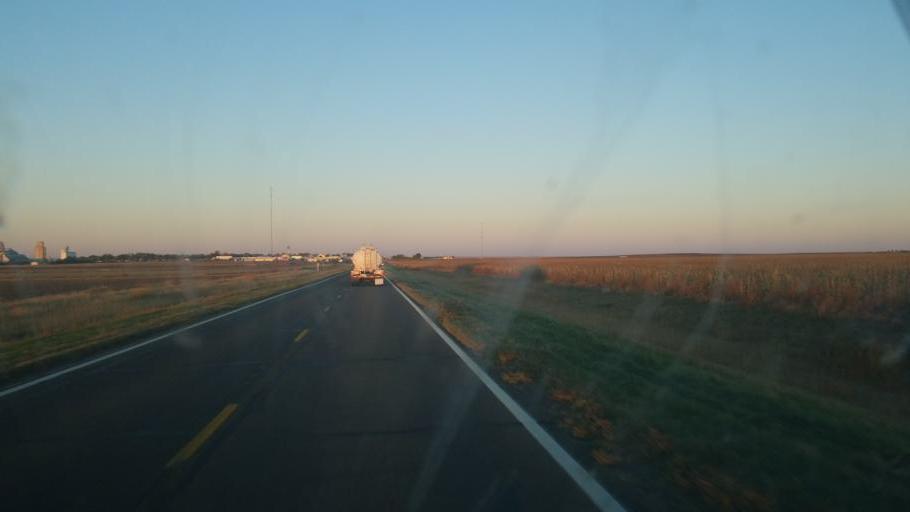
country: US
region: Kansas
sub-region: Wallace County
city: Sharon Springs
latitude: 38.9019
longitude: -101.7284
